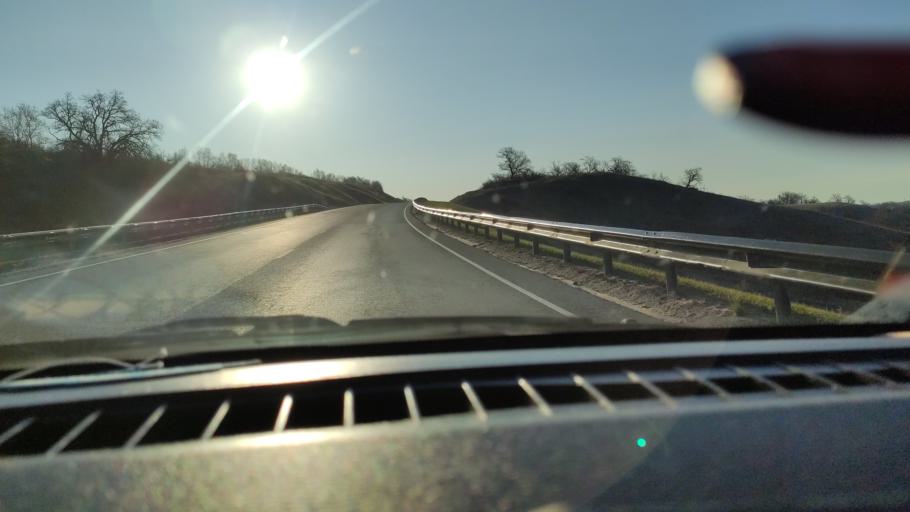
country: RU
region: Saratov
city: Tersa
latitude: 52.1037
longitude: 47.4913
